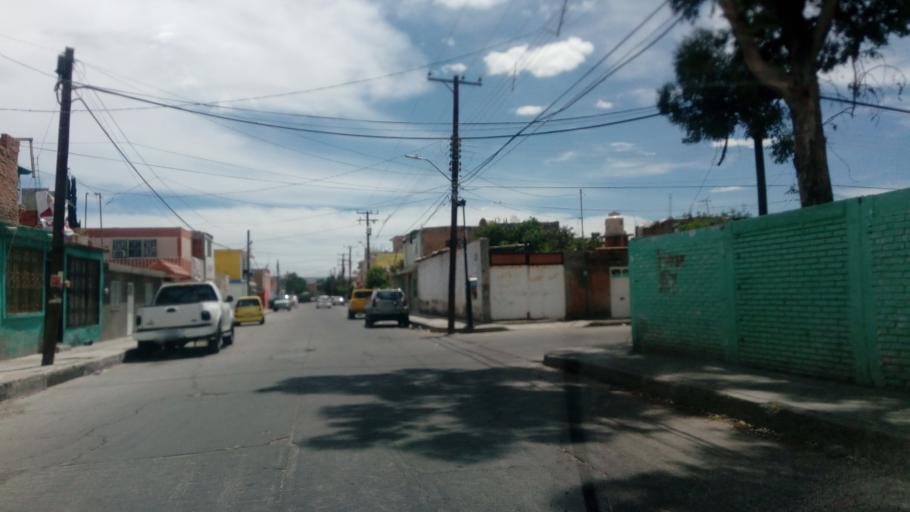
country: MX
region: Durango
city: Victoria de Durango
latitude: 24.0046
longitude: -104.6773
